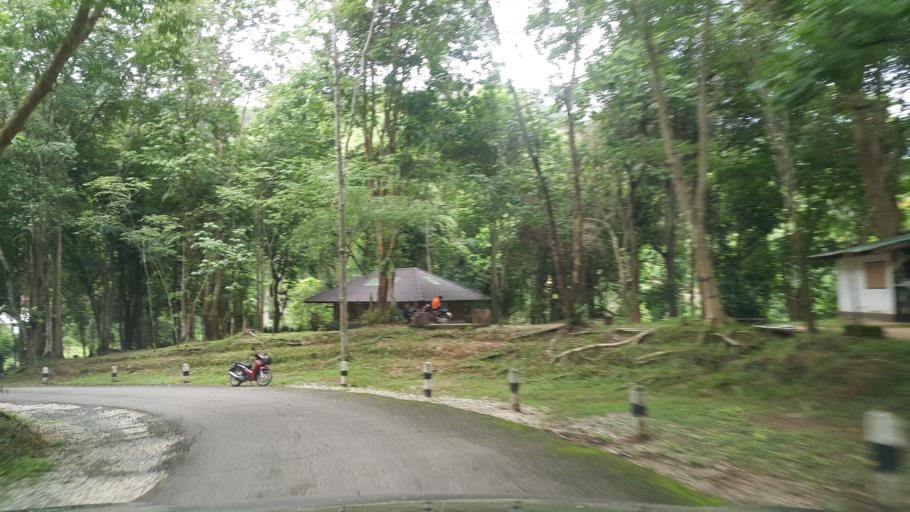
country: TH
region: Phitsanulok
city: Chat Trakan
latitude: 17.3007
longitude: 100.6787
